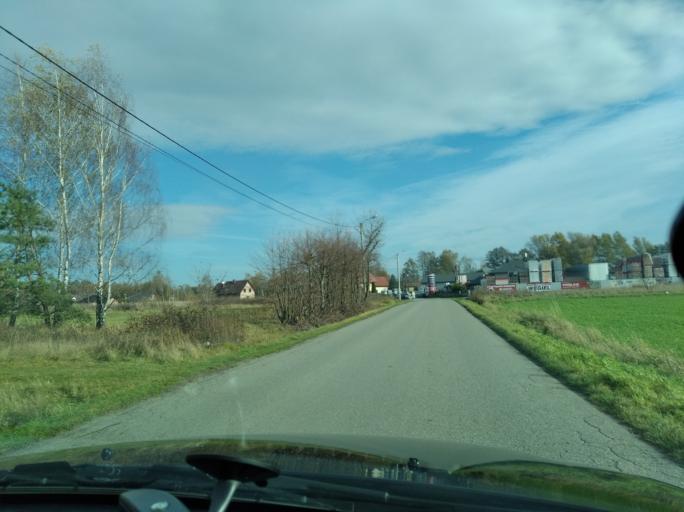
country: PL
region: Subcarpathian Voivodeship
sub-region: Powiat ropczycko-sedziszowski
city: Sedziszow Malopolski
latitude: 50.0984
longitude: 21.6573
